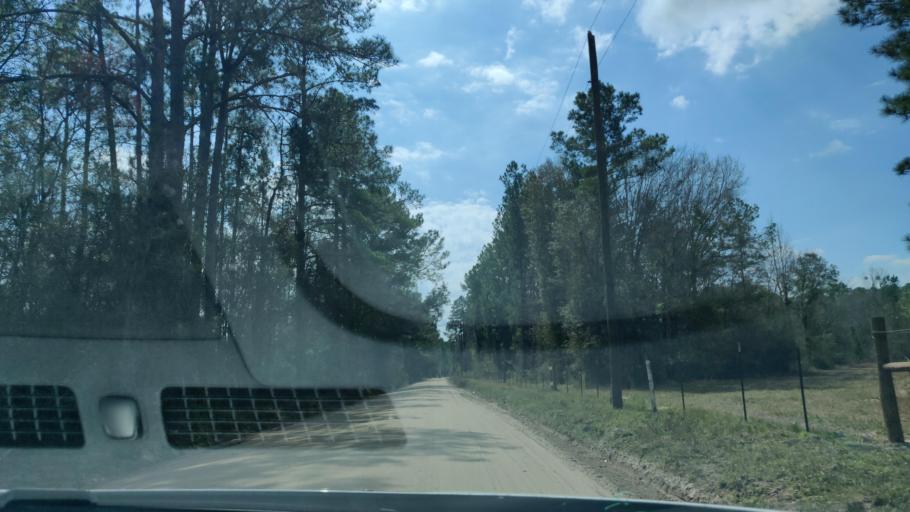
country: US
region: Florida
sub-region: Duval County
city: Baldwin
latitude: 30.1850
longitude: -81.9701
